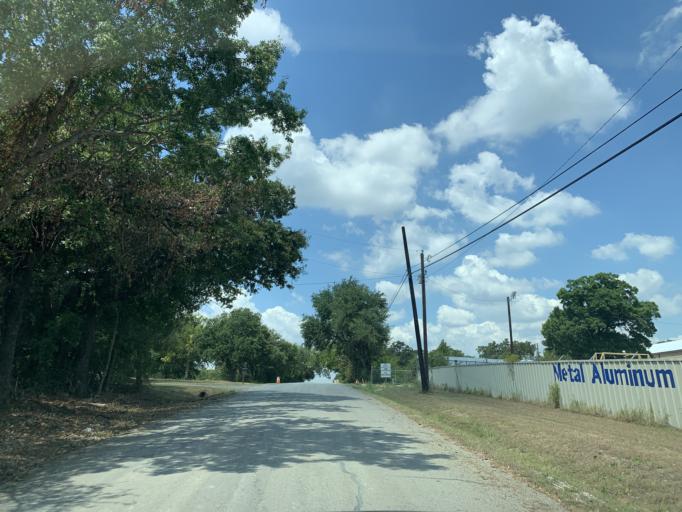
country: US
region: Texas
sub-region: Tarrant County
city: Lakeside
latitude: 32.8417
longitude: -97.4997
